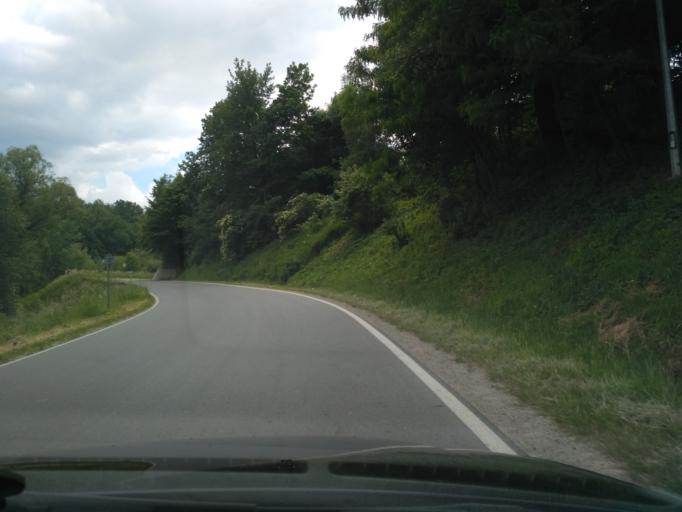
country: PL
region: Subcarpathian Voivodeship
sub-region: Powiat przeworski
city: Jawornik Polski
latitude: 49.8952
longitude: 22.2938
